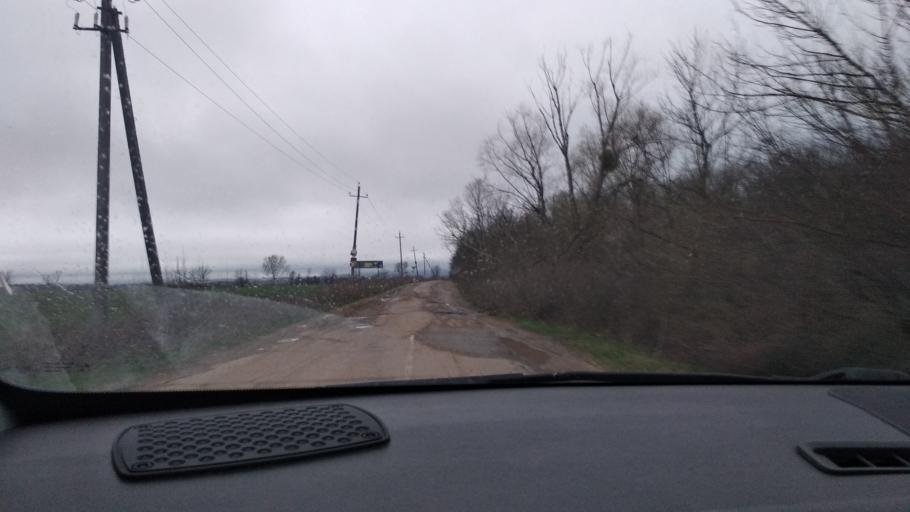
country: RU
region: Krasnodarskiy
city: Afipskiy
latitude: 44.9042
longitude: 38.7693
